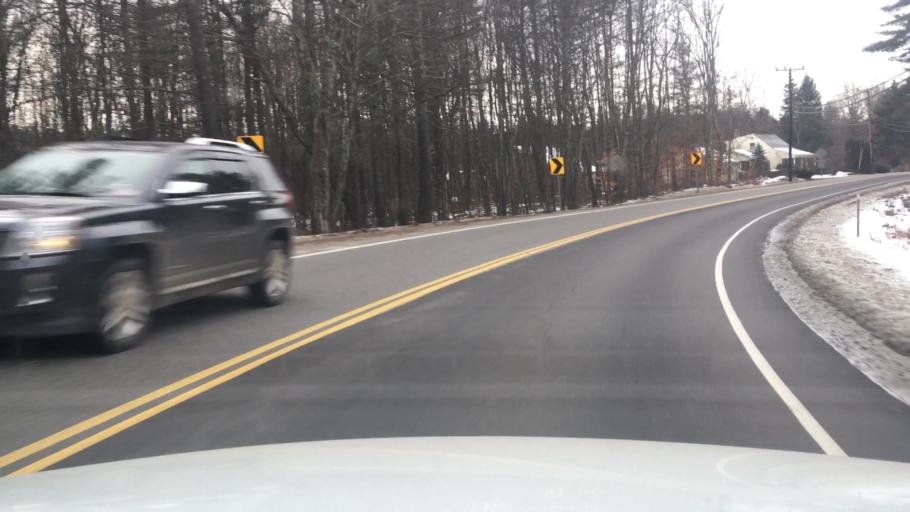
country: US
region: New Hampshire
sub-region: Merrimack County
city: Concord
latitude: 43.1568
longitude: -71.5976
